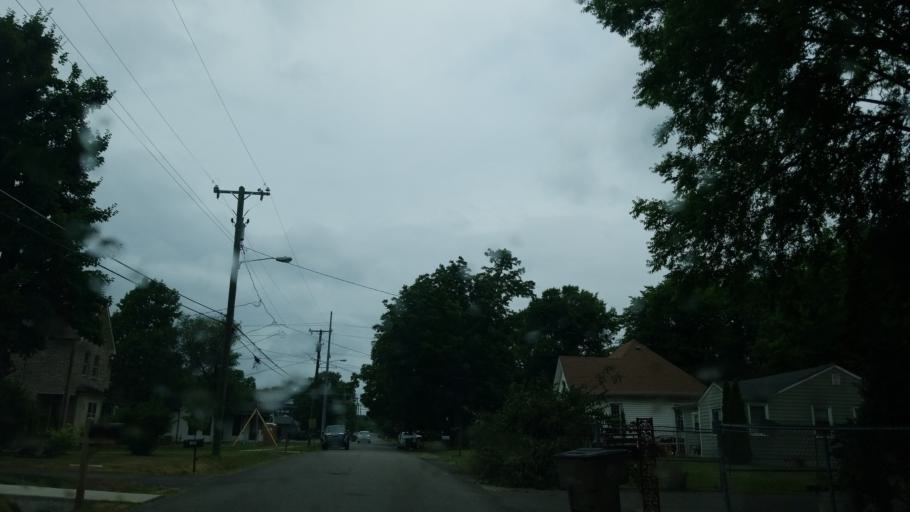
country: US
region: Tennessee
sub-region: Davidson County
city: Nashville
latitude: 36.1375
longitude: -86.7683
